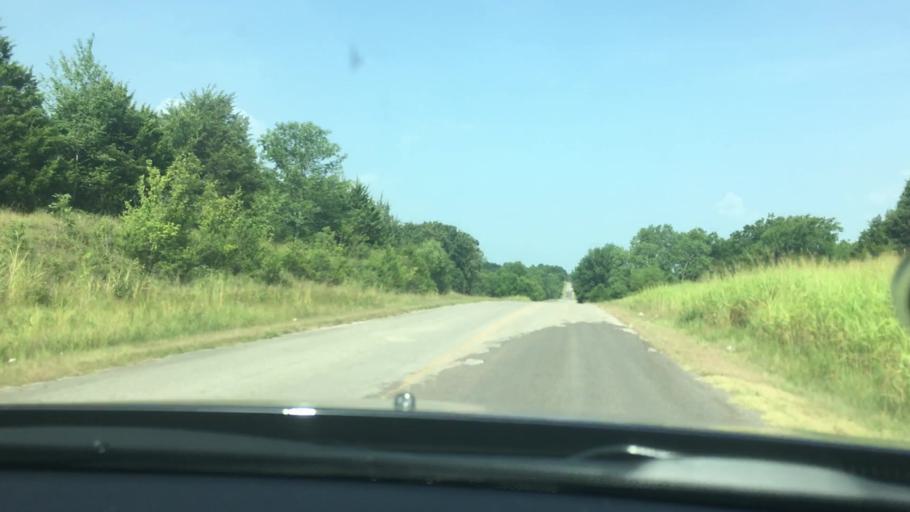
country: US
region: Oklahoma
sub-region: Pontotoc County
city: Byng
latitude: 34.8737
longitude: -96.5798
